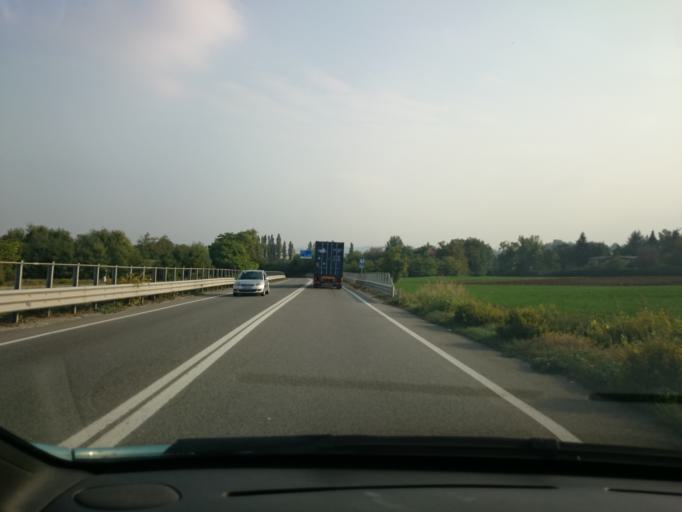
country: IT
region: Emilia-Romagna
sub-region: Provincia di Reggio Emilia
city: Veggia-Villalunga
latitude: 44.5636
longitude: 10.7580
